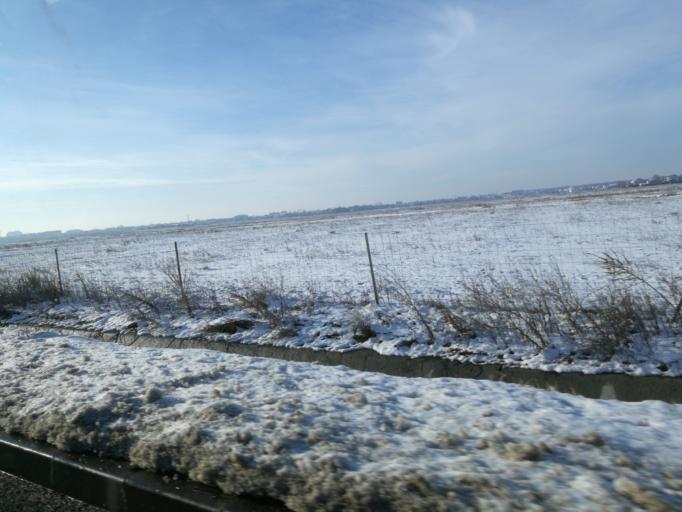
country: RO
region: Ilfov
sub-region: Voluntari City
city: Voluntari
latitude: 44.5069
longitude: 26.1606
